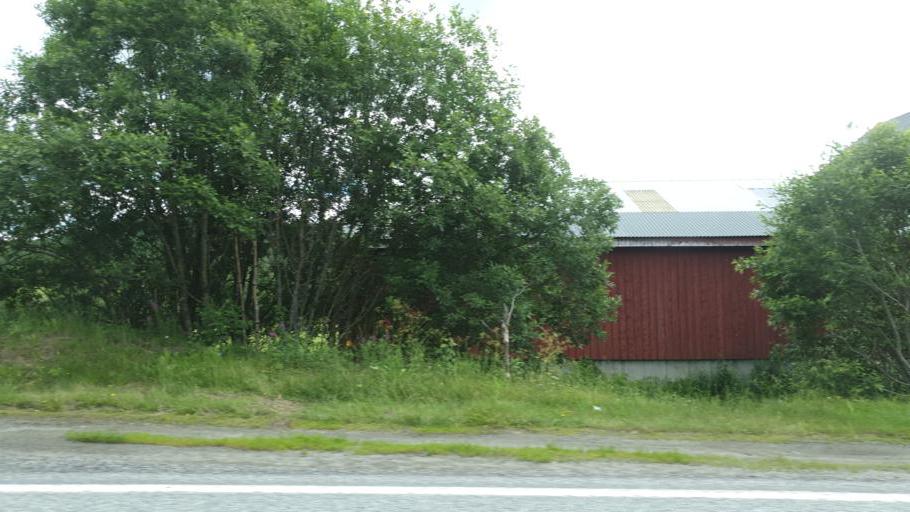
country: NO
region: Sor-Trondelag
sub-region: Rennebu
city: Berkak
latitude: 62.8796
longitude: 10.0910
